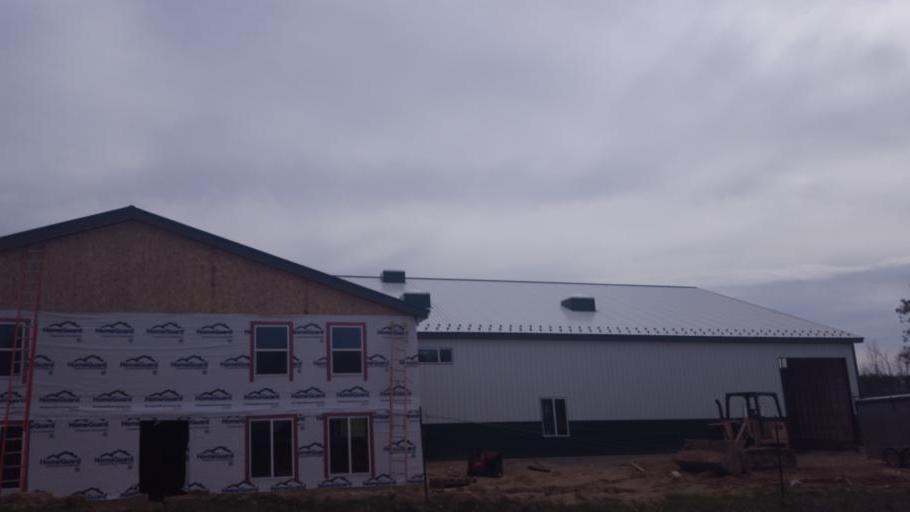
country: US
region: Michigan
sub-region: Clare County
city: Clare
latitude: 43.8729
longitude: -84.7261
